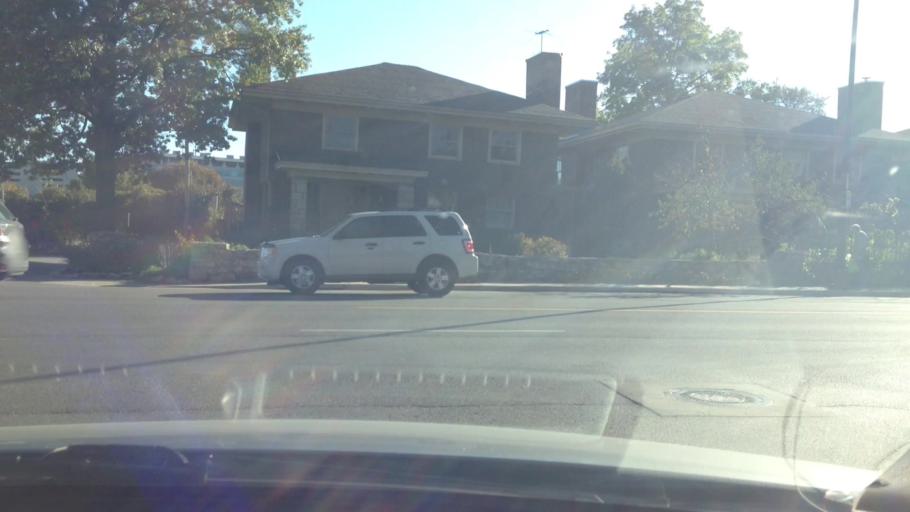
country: US
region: Kansas
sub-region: Johnson County
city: Westwood
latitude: 39.0419
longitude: -94.5742
